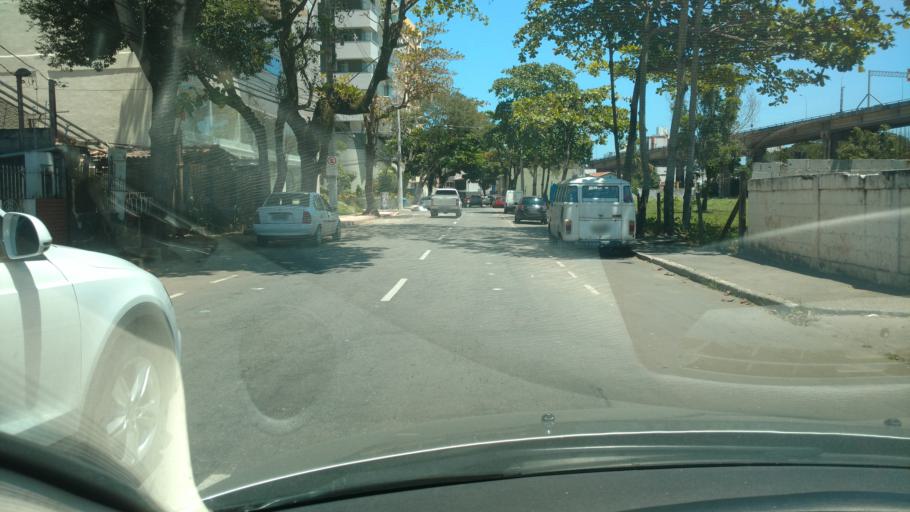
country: BR
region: Espirito Santo
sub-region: Vila Velha
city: Vila Velha
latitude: -20.3314
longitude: -40.2823
